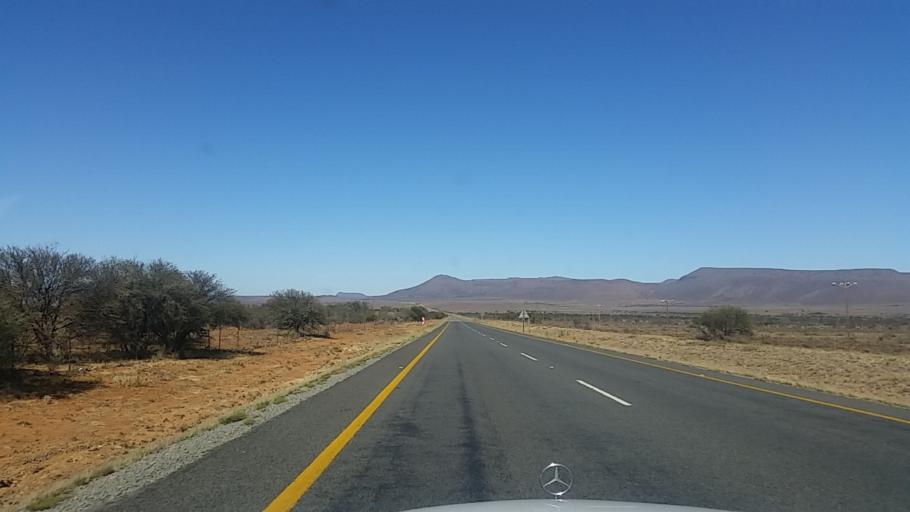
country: ZA
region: Eastern Cape
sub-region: Cacadu District Municipality
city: Graaff-Reinet
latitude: -31.9922
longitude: 24.6813
